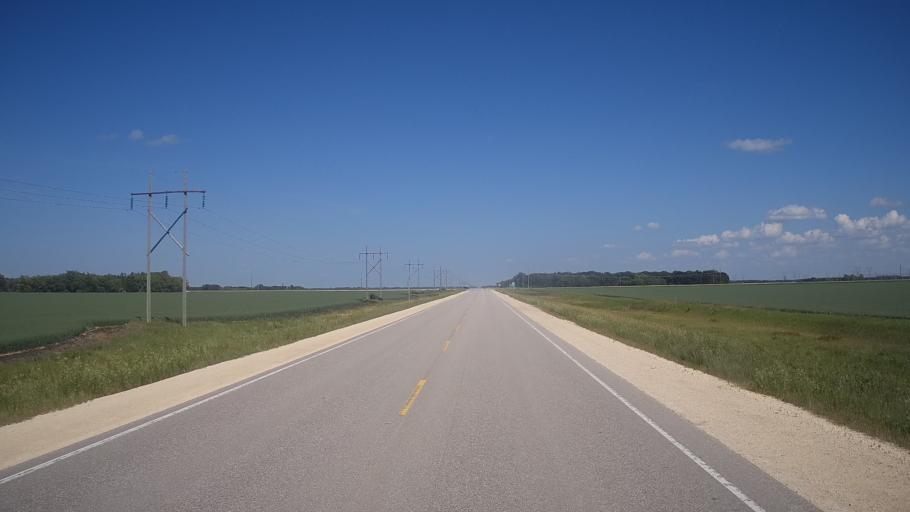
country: CA
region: Manitoba
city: Stonewall
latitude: 50.1227
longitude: -97.4448
